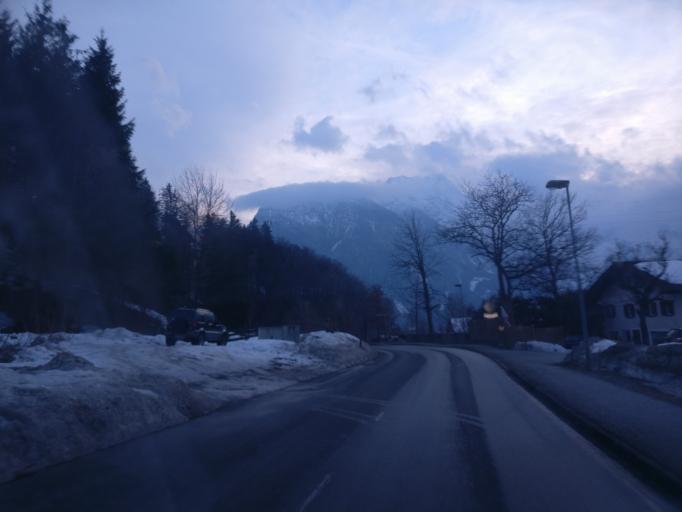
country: AT
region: Salzburg
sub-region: Politischer Bezirk Hallein
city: Golling an der Salzach
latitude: 47.6172
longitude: 13.1714
